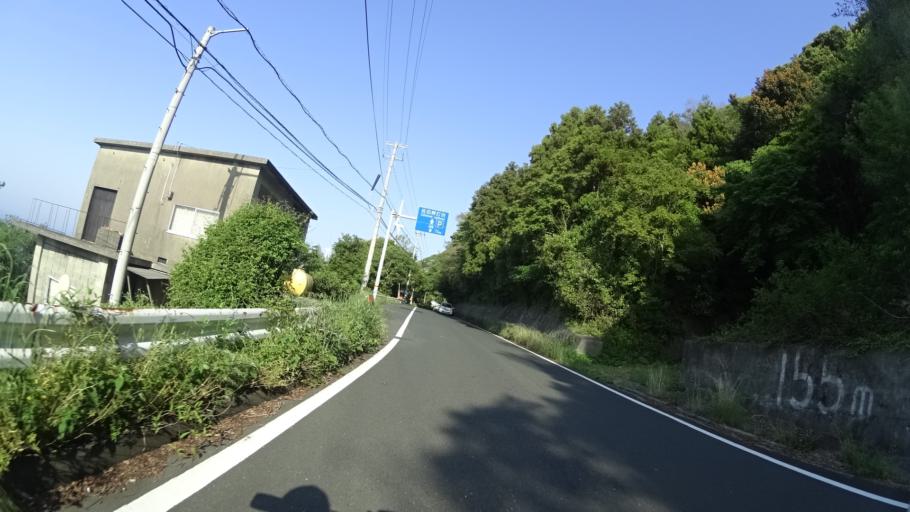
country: JP
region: Ehime
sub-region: Nishiuwa-gun
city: Ikata-cho
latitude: 33.3835
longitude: 132.0823
